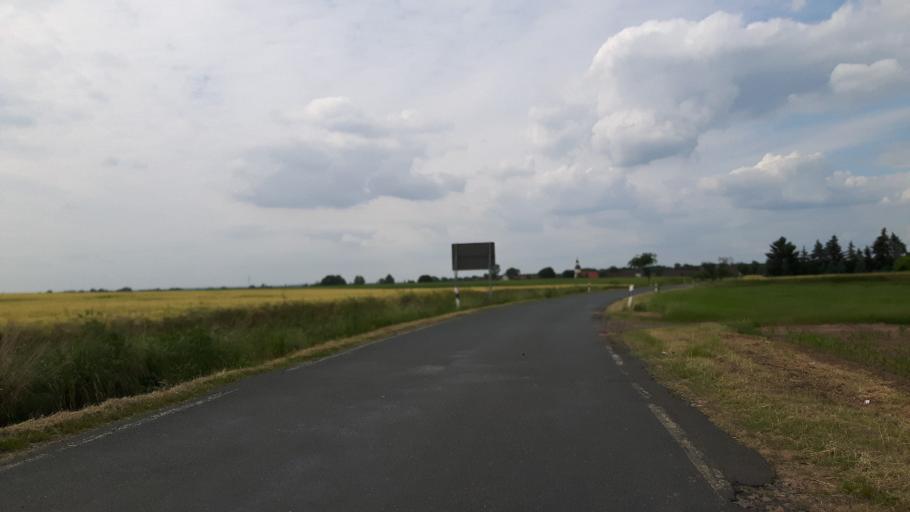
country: DE
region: Saxony-Anhalt
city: Bergwitz
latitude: 51.8103
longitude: 12.5726
